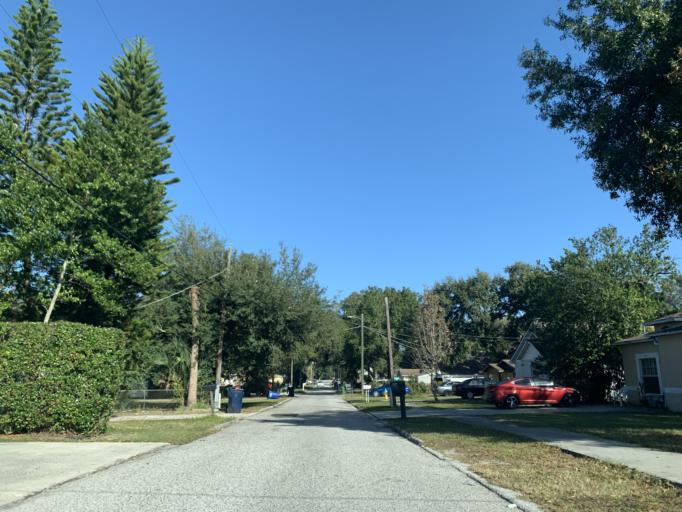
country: US
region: Florida
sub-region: Hillsborough County
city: Temple Terrace
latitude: 28.0298
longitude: -82.4116
